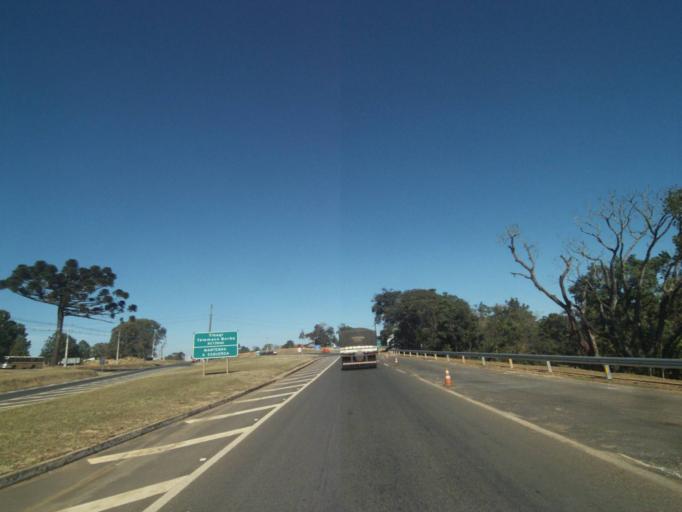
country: BR
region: Parana
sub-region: Reserva
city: Reserva
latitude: -24.6275
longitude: -50.6439
